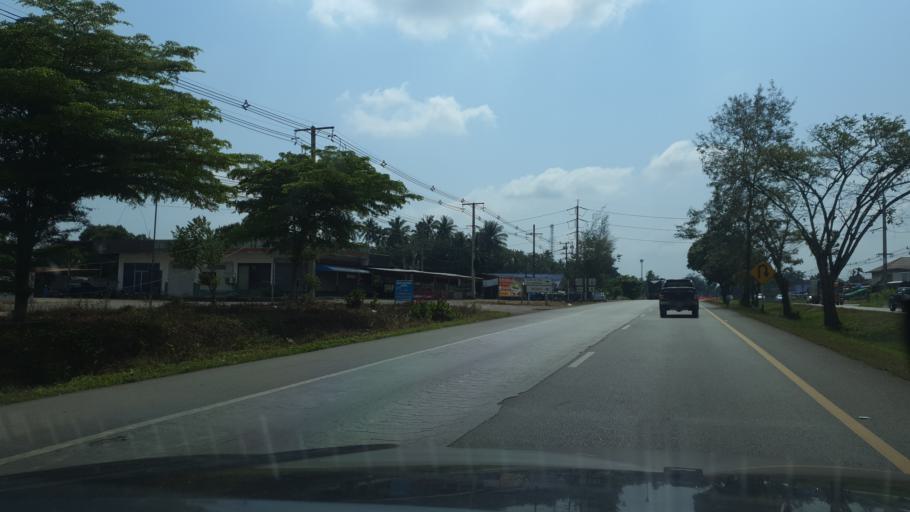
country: TH
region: Chumphon
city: Chumphon
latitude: 10.4024
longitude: 99.1283
